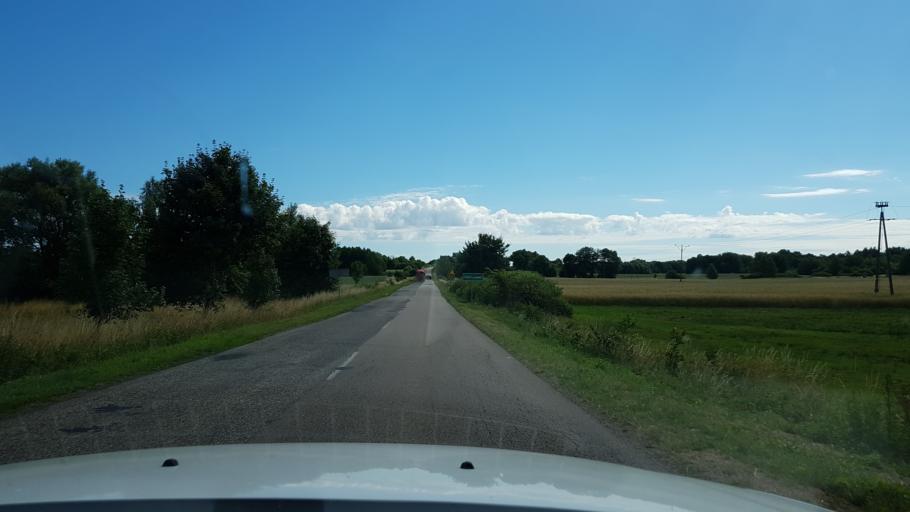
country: PL
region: West Pomeranian Voivodeship
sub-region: Powiat gryficki
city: Cerkwica
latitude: 54.0342
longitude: 15.1866
